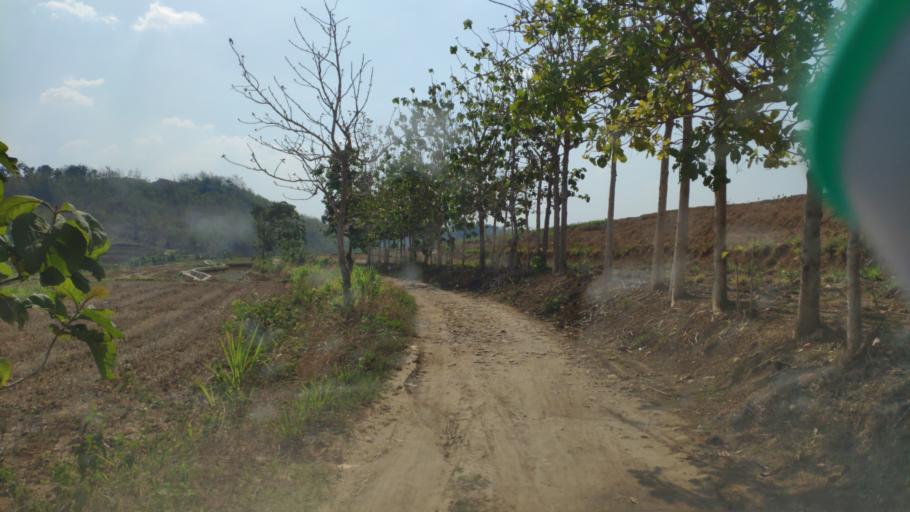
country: ID
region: Central Java
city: Ngapus
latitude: -6.9344
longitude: 111.2156
